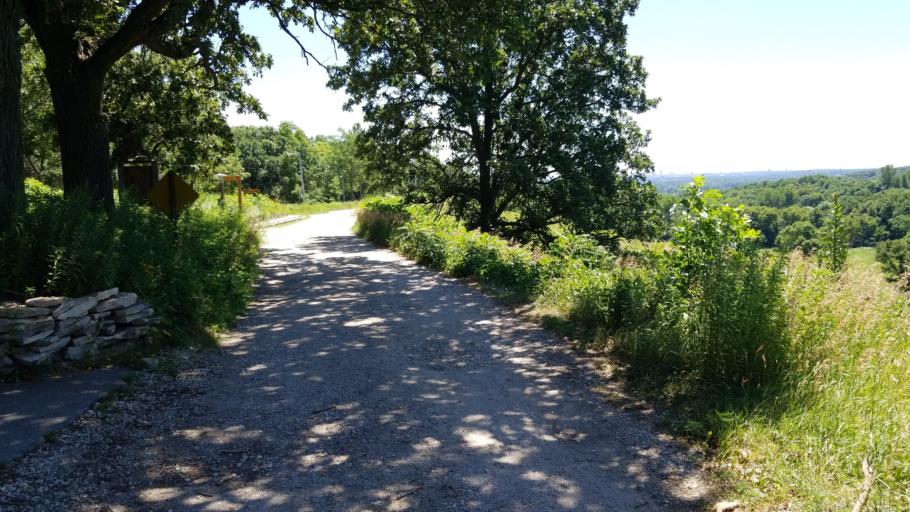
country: US
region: Iowa
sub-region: Pottawattamie County
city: Carter Lake
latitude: 41.3899
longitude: -95.9520
